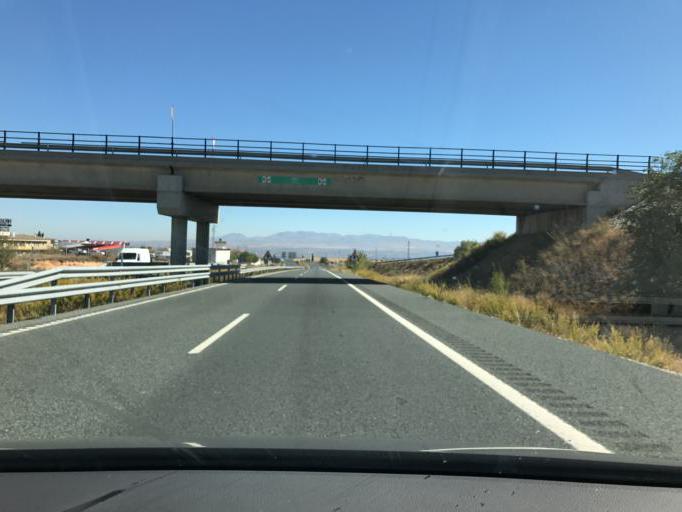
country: ES
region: Andalusia
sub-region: Provincia de Granada
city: Darro
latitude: 37.3216
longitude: -3.2701
